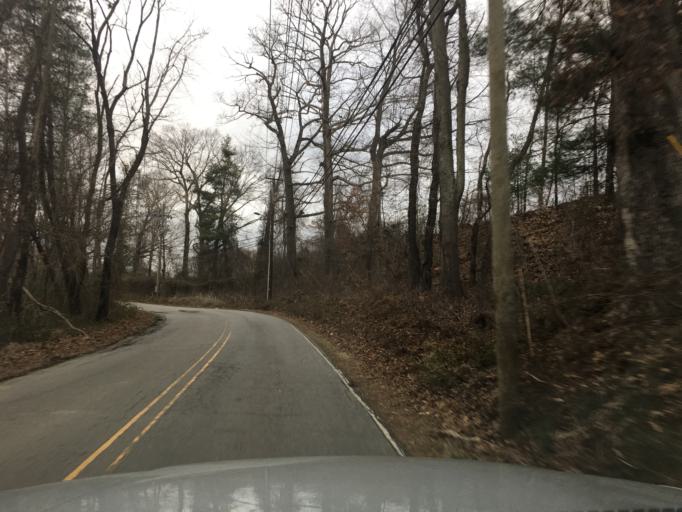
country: US
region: North Carolina
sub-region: Buncombe County
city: Asheville
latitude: 35.5995
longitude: -82.5831
